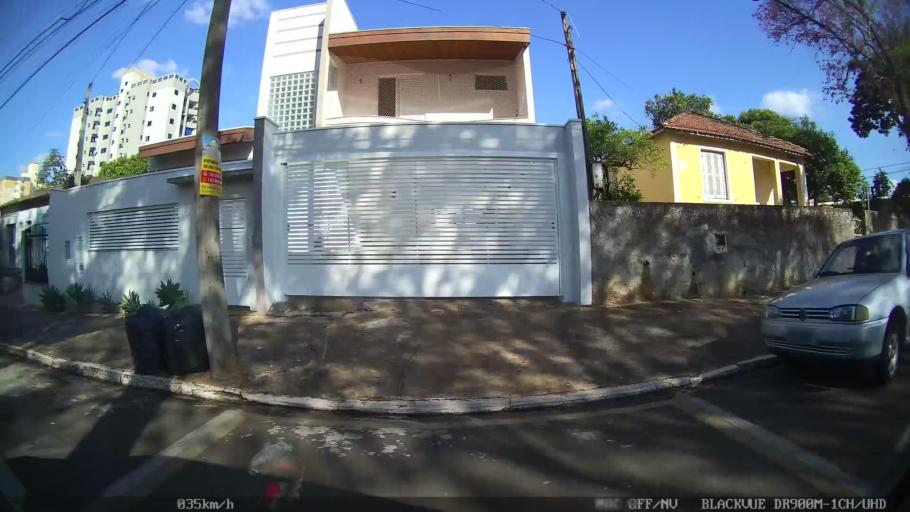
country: BR
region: Sao Paulo
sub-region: Nova Odessa
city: Nova Odessa
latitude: -22.7790
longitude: -47.2965
